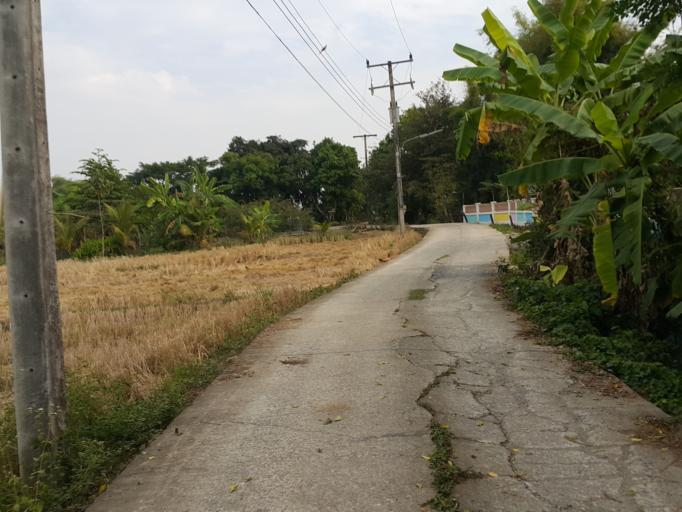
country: TH
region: Chiang Mai
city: San Kamphaeng
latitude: 18.8252
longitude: 99.1435
